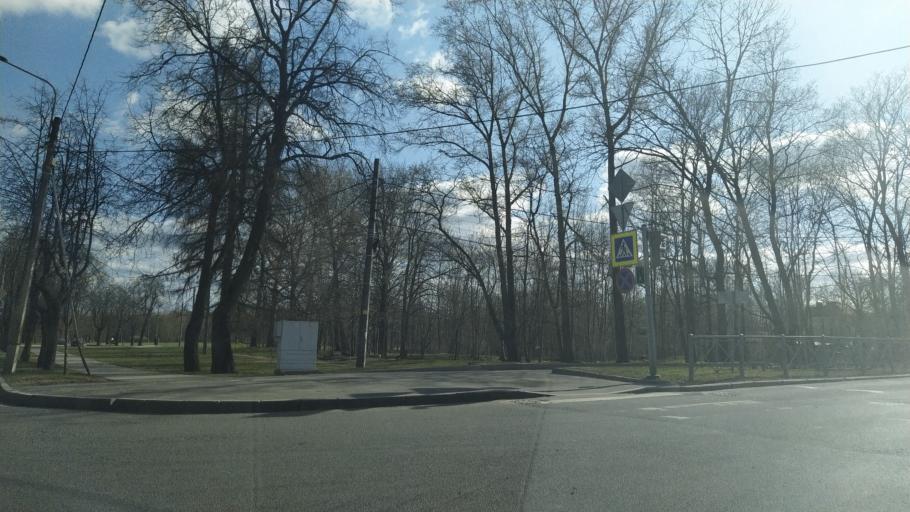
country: RU
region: St.-Petersburg
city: Pushkin
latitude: 59.7037
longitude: 30.4192
